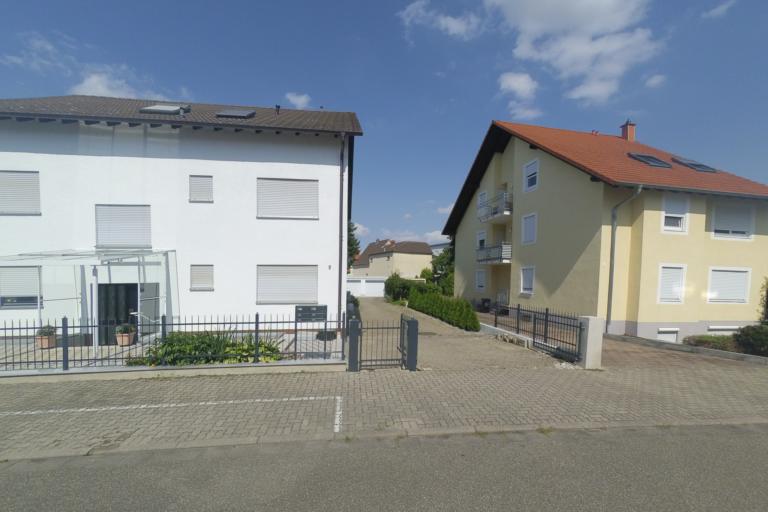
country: DE
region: Rheinland-Pfalz
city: Schifferstadt
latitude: 49.3814
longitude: 8.3801
